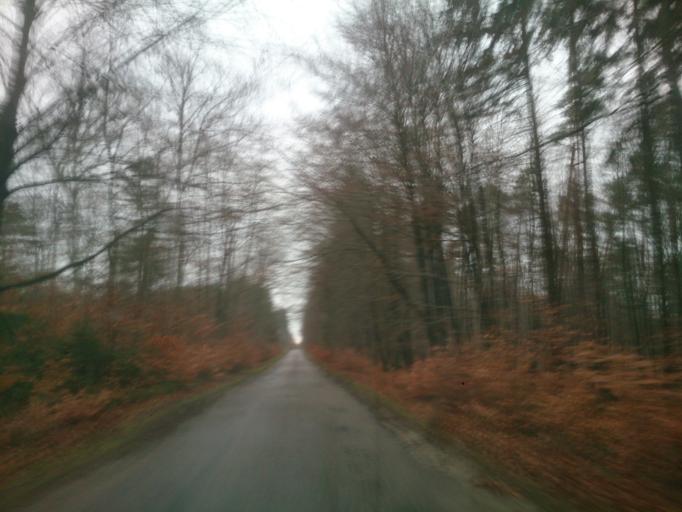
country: PL
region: Pomeranian Voivodeship
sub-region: Powiat slupski
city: Kepice
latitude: 54.1954
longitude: 16.8384
